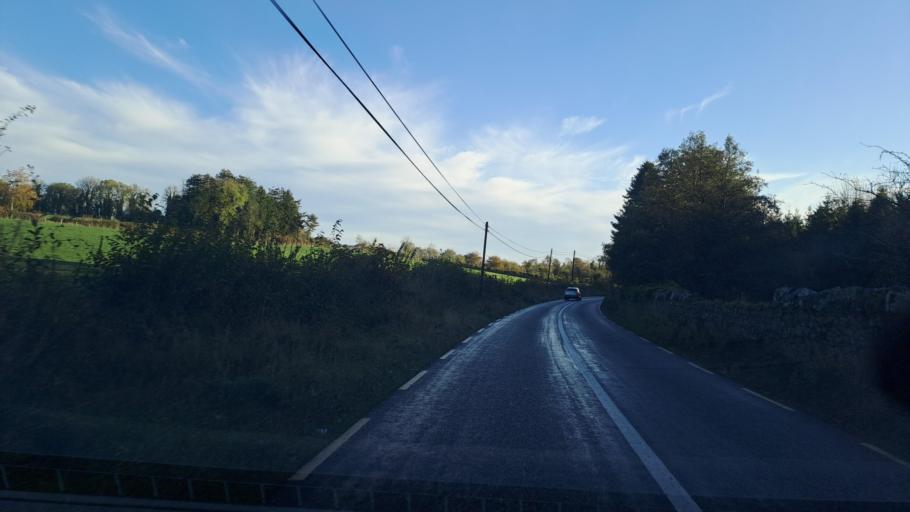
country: IE
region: Ulster
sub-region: An Cabhan
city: Cootehill
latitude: 54.1131
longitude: -7.0412
